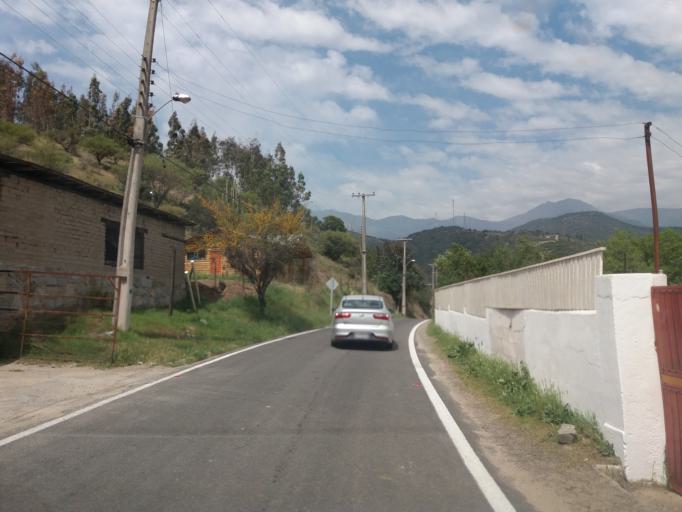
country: CL
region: Valparaiso
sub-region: Provincia de Marga Marga
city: Limache
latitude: -33.0456
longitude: -71.0994
